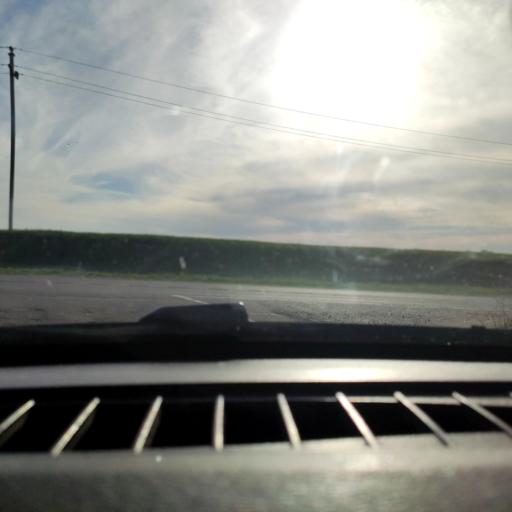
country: RU
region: Belgorod
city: Staryy Oskol
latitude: 51.3442
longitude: 37.7937
